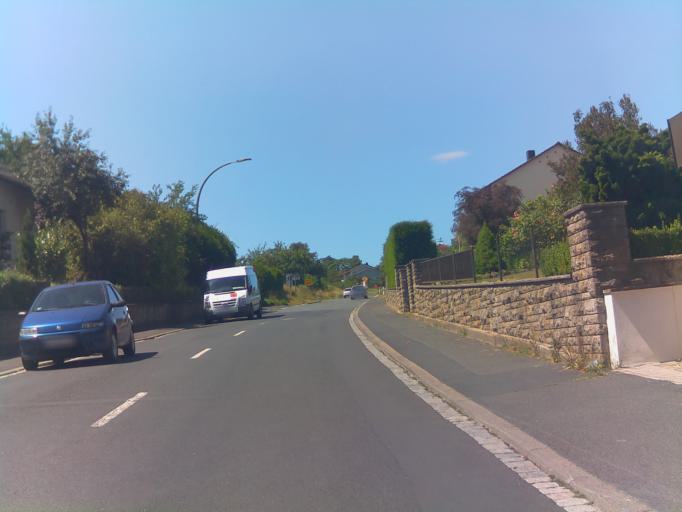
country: DE
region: Bavaria
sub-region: Regierungsbezirk Unterfranken
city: Rimpar
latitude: 49.8581
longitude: 9.9493
